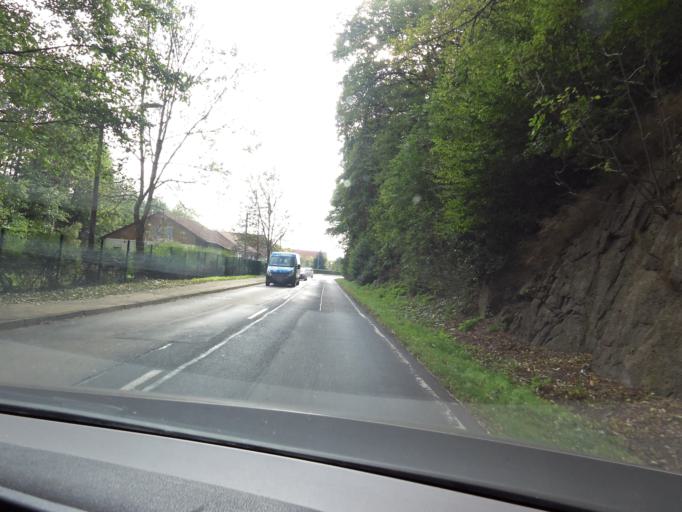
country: DE
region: Thuringia
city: Trusetal
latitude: 50.7820
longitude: 10.4061
